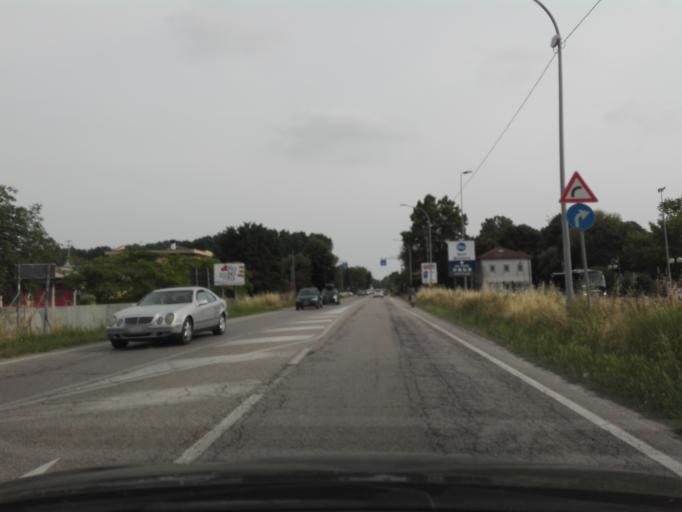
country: IT
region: Veneto
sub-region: Provincia di Rovigo
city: Rovigo
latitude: 45.0855
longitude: 11.7853
